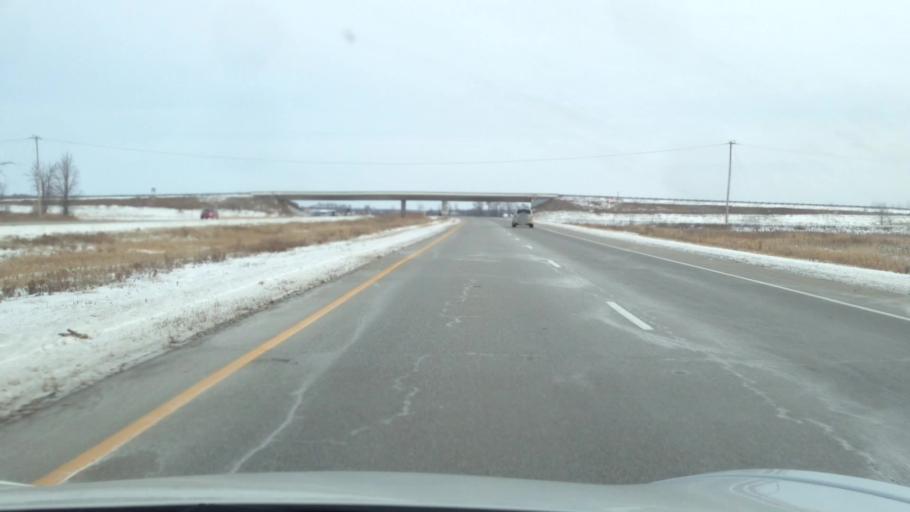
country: CA
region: Ontario
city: Casselman
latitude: 45.3417
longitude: -74.9037
